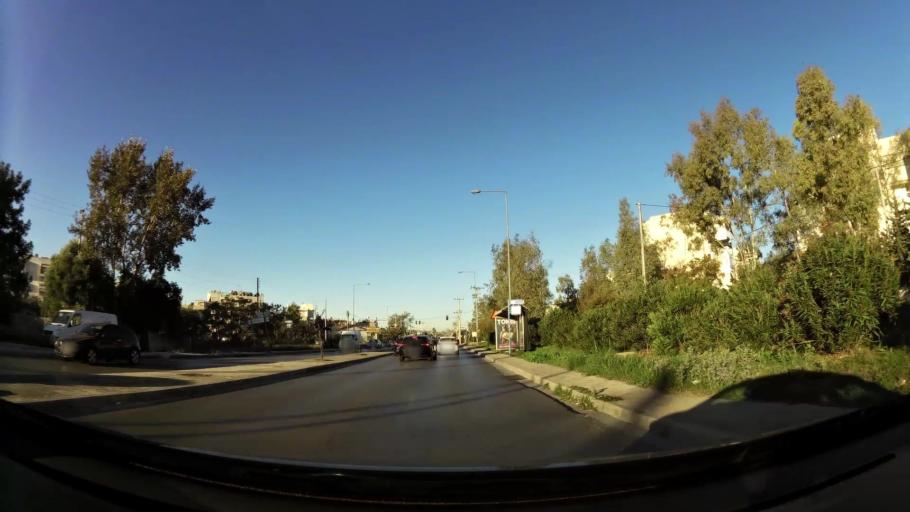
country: GR
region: Attica
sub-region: Nomarchia Athinas
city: Agia Paraskevi
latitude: 38.0232
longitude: 23.8283
